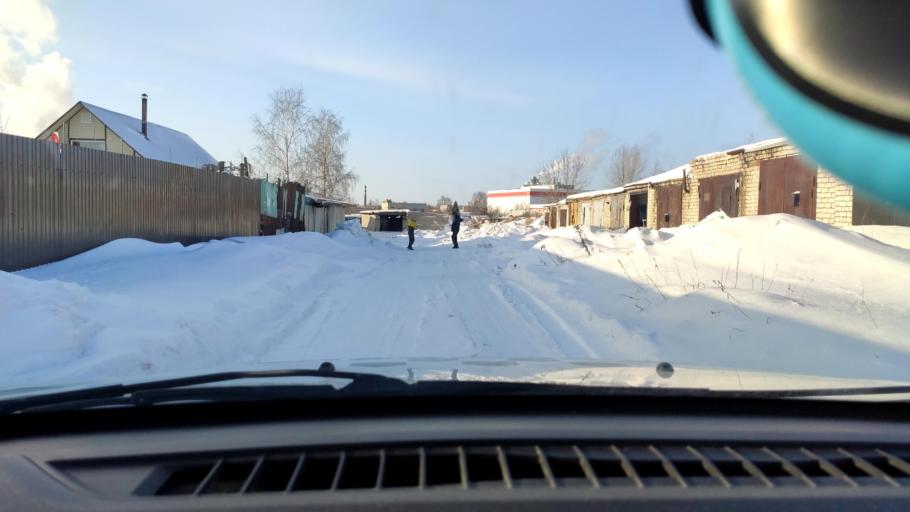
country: RU
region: Perm
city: Overyata
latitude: 58.0177
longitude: 55.9365
